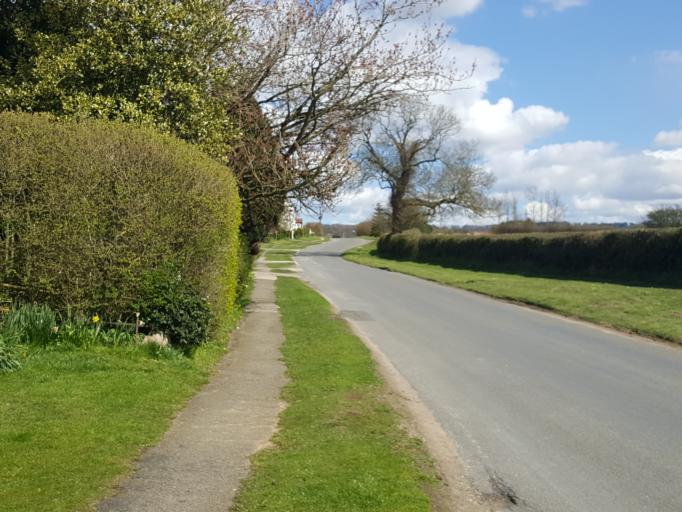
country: GB
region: England
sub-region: East Riding of Yorkshire
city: Ellerker
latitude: 53.7529
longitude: -0.6009
